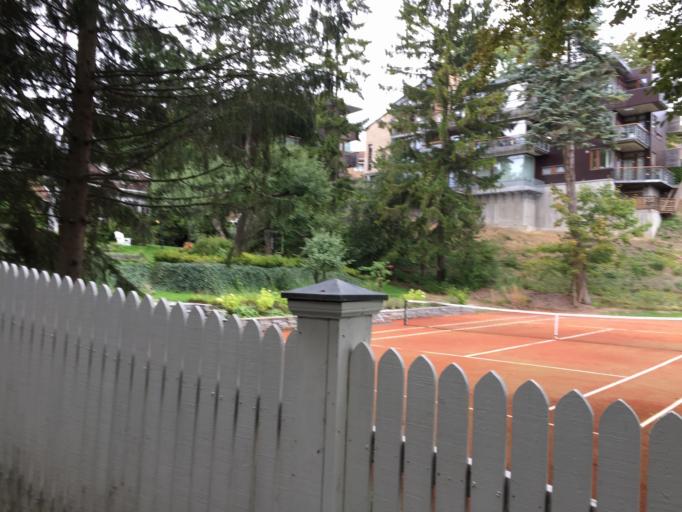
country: NO
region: Oslo
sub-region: Oslo
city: Sjolyststranda
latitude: 59.9021
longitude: 10.6887
